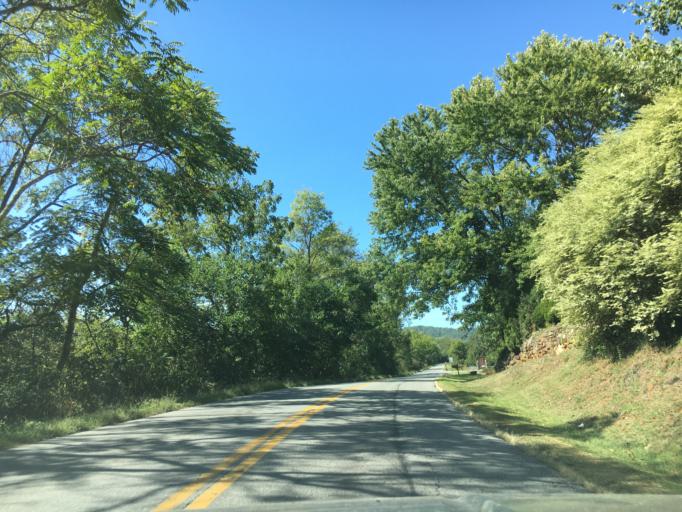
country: US
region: Virginia
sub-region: Albemarle County
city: Crozet
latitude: 37.9571
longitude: -78.6604
